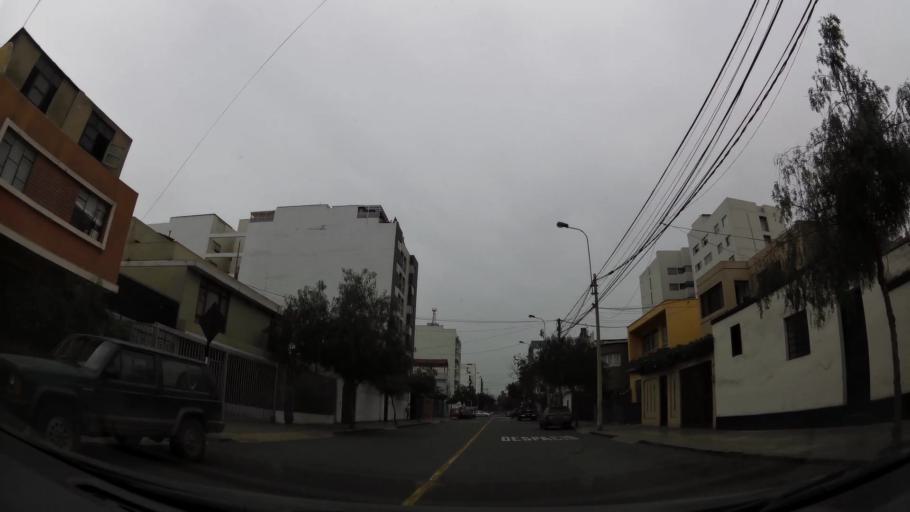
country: PE
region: Lima
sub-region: Lima
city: San Isidro
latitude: -12.1167
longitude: -77.0313
